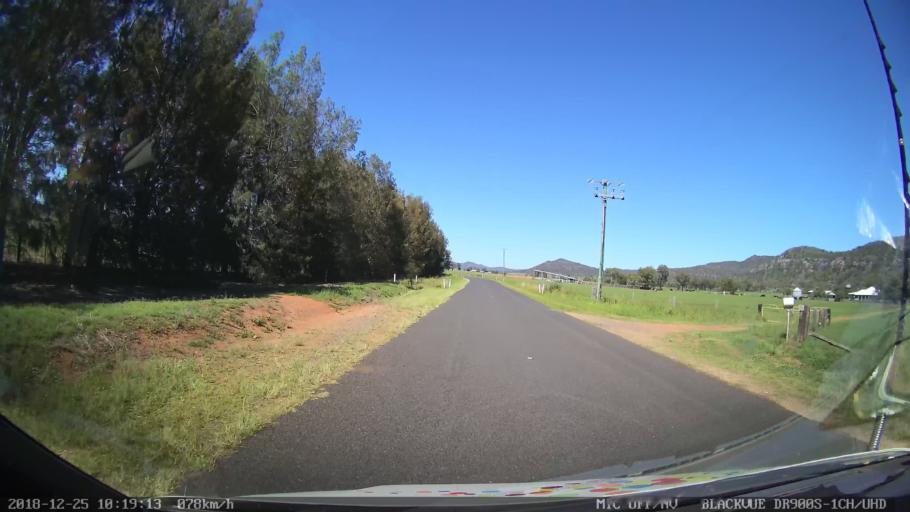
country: AU
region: New South Wales
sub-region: Muswellbrook
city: Denman
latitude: -32.3488
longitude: 150.5604
